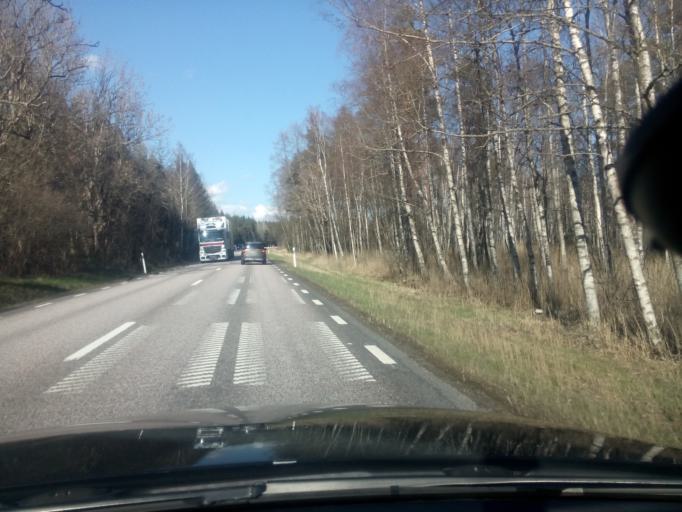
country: SE
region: Soedermanland
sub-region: Flens Kommun
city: Malmkoping
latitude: 59.2101
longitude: 16.8484
